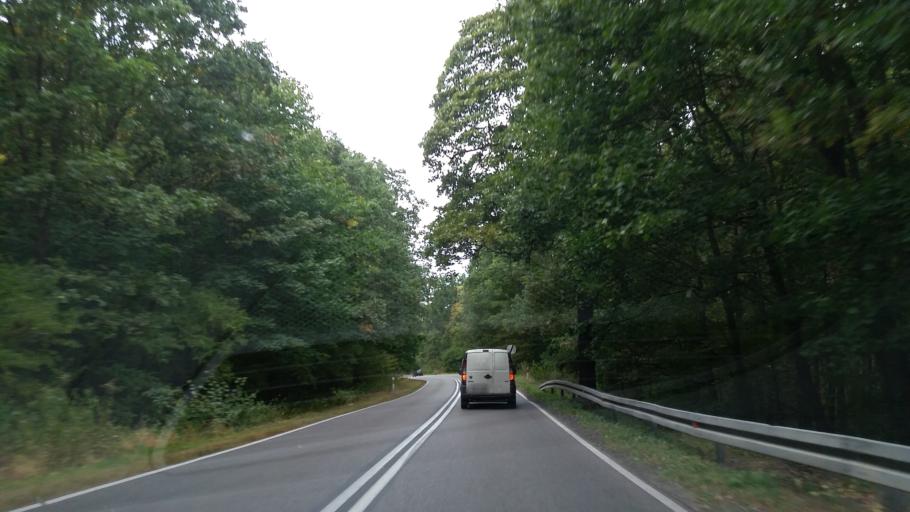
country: PL
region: West Pomeranian Voivodeship
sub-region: Powiat mysliborski
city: Barlinek
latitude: 53.0026
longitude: 15.2423
